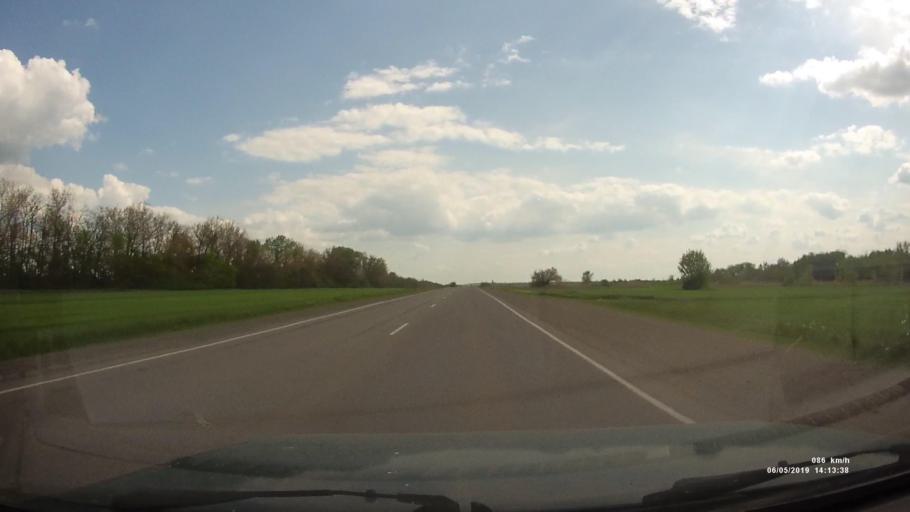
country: RU
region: Rostov
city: Kamenolomni
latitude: 47.6583
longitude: 40.2931
